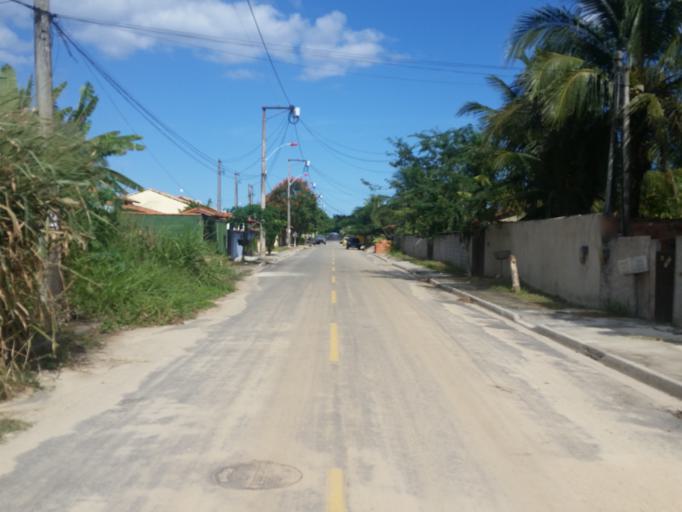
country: BR
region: Rio de Janeiro
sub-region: Marica
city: Marica
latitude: -22.9599
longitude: -42.9667
